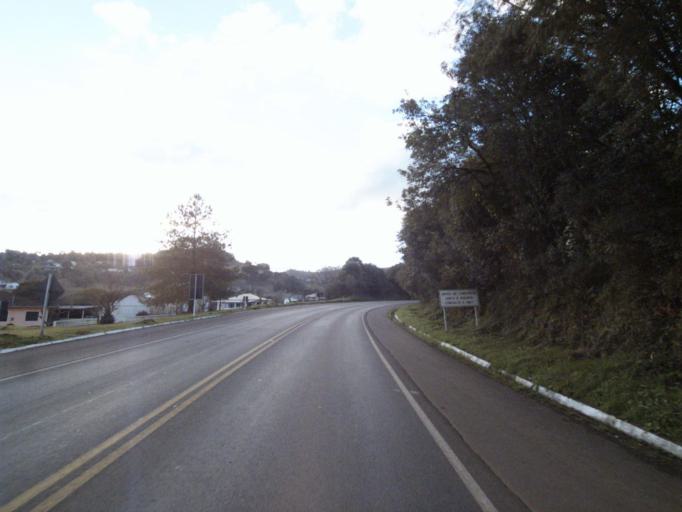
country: BR
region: Santa Catarina
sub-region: Joacaba
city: Joacaba
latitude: -27.2735
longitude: -51.4425
